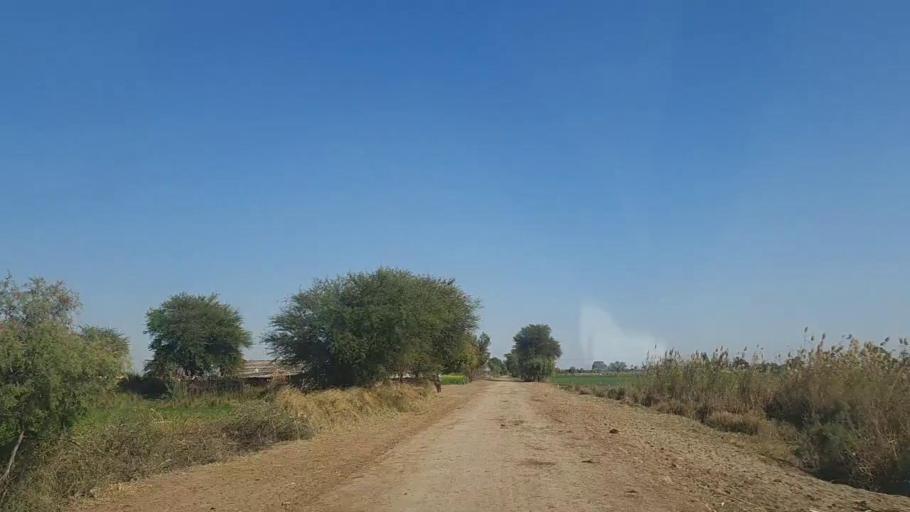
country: PK
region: Sindh
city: Sanghar
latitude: 26.2204
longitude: 68.9648
